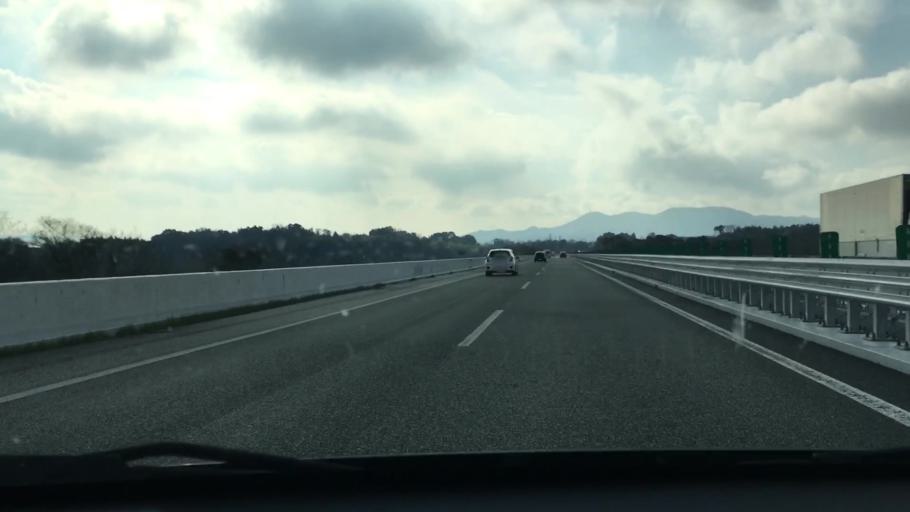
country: JP
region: Kumamoto
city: Uto
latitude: 32.7106
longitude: 130.7632
